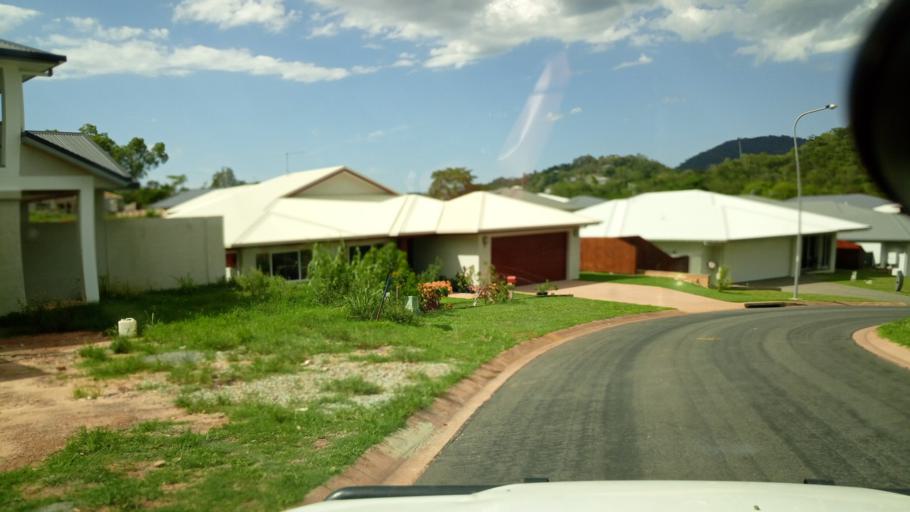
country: AU
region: Queensland
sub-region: Cairns
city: Woree
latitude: -16.9226
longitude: 145.7222
